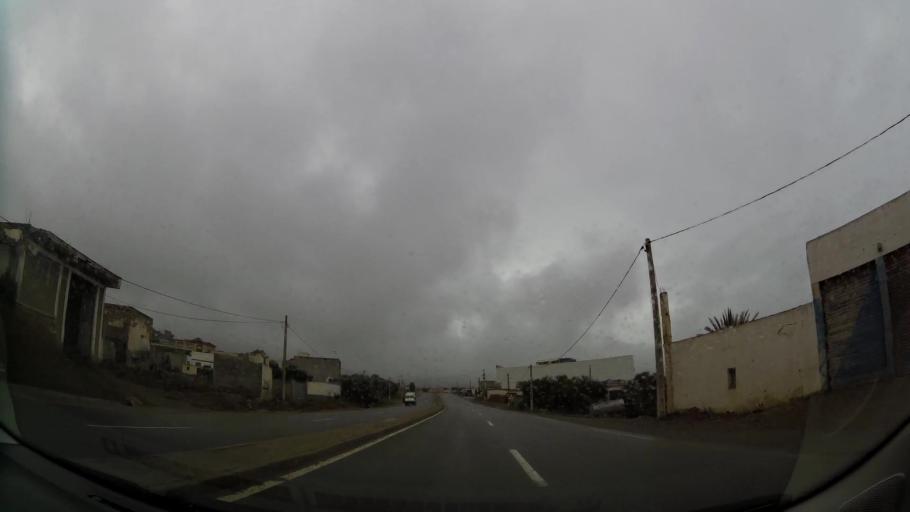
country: MA
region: Taza-Al Hoceima-Taounate
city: Imzourene
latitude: 35.1916
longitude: -3.8888
